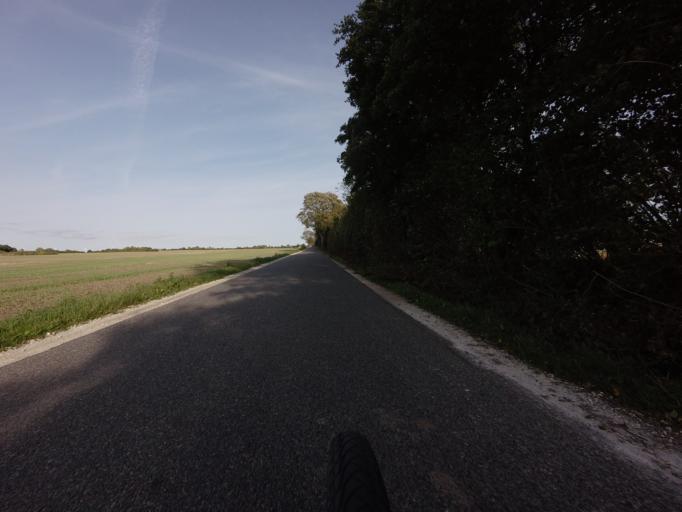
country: DK
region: Zealand
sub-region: Faxe Kommune
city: Fakse Ladeplads
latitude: 55.2528
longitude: 12.2376
